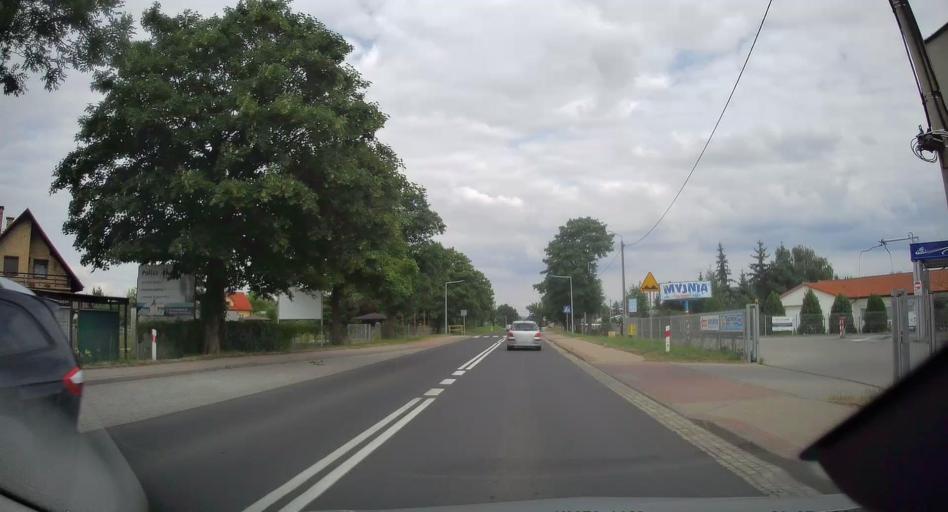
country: PL
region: Lower Silesian Voivodeship
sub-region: Powiat swidnicki
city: Swidnica
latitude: 50.8401
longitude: 16.4397
